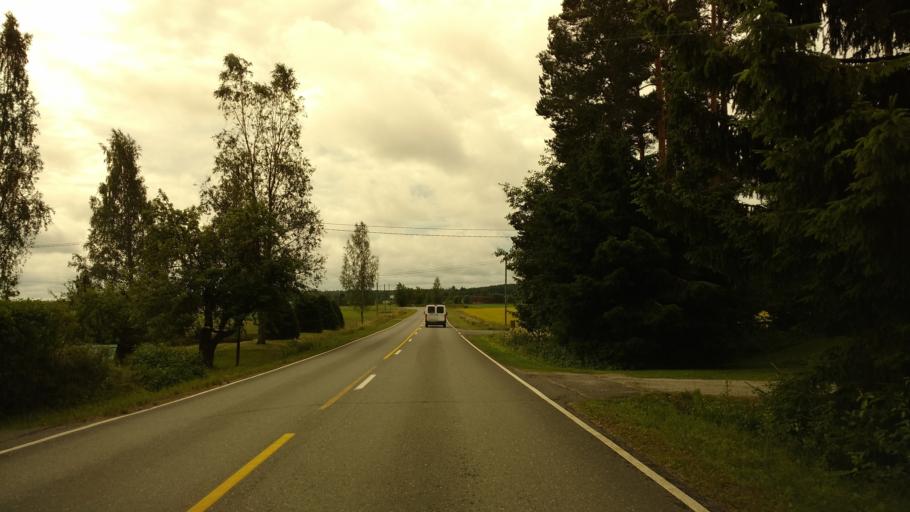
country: FI
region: Varsinais-Suomi
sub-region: Salo
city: Kuusjoki
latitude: 60.5468
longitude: 23.1626
